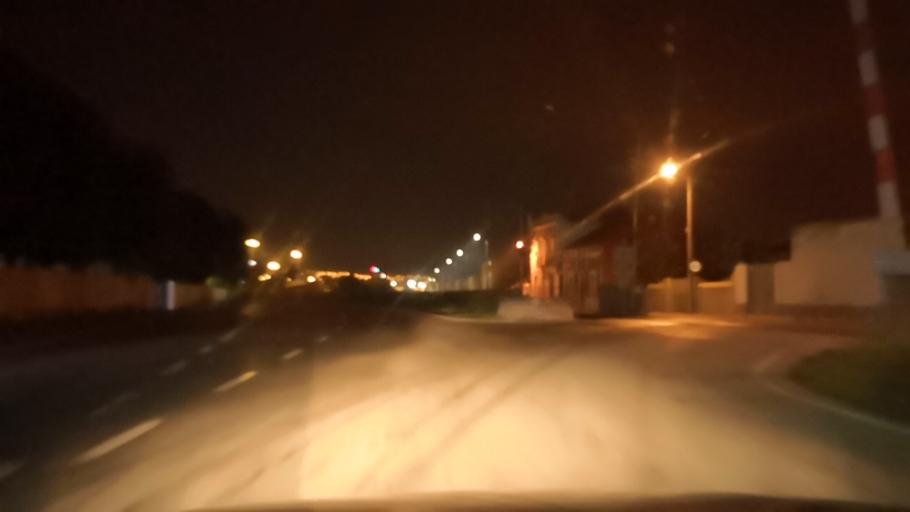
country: PT
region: Setubal
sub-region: Setubal
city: Setubal
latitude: 38.5128
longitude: -8.8590
